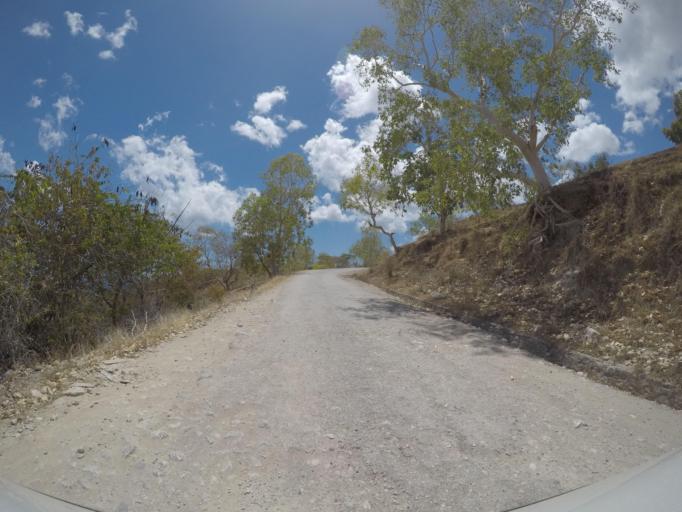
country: TL
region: Baucau
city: Baucau
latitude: -8.4831
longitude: 126.6106
